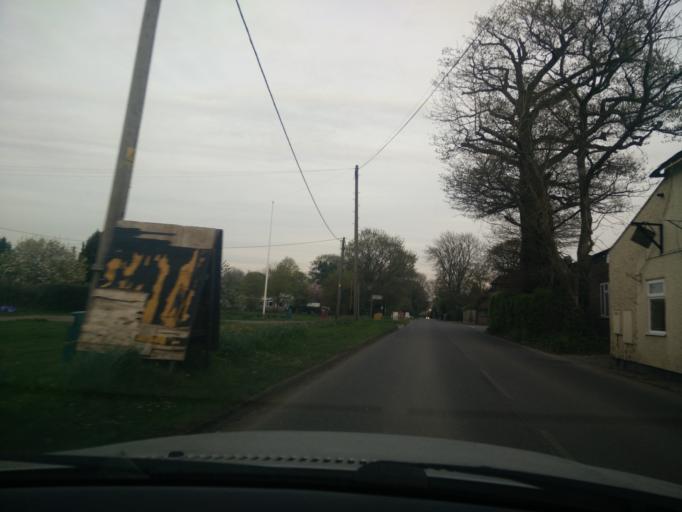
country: GB
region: England
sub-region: Buckinghamshire
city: Amersham
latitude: 51.6943
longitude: -0.6553
